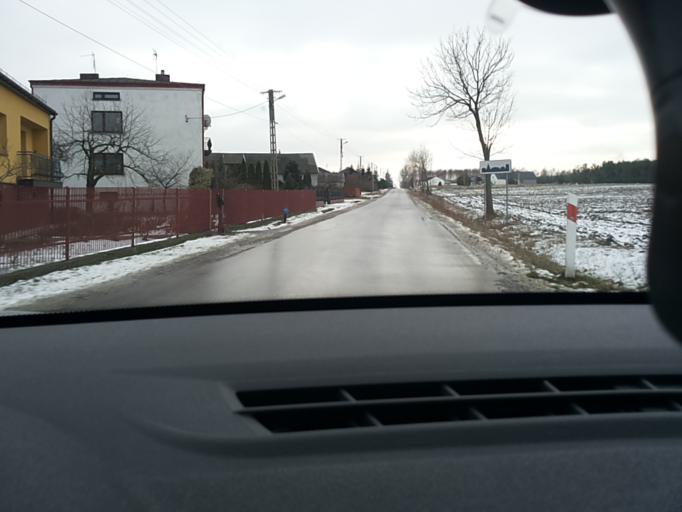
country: PL
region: Lodz Voivodeship
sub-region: powiat Lowicki
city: Nieborow
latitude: 52.0127
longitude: 20.0661
